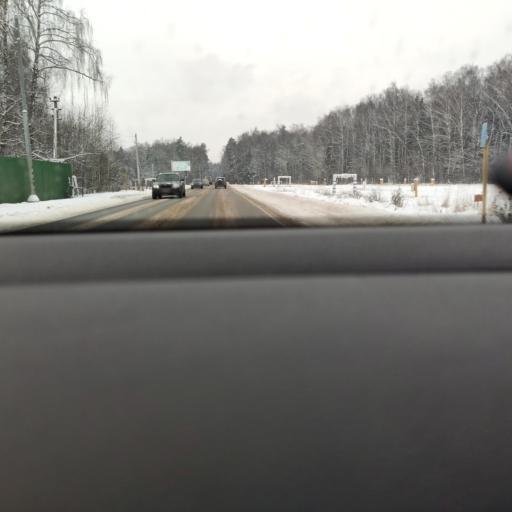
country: RU
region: Moskovskaya
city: Andreyevskoye
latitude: 55.5192
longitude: 37.9120
